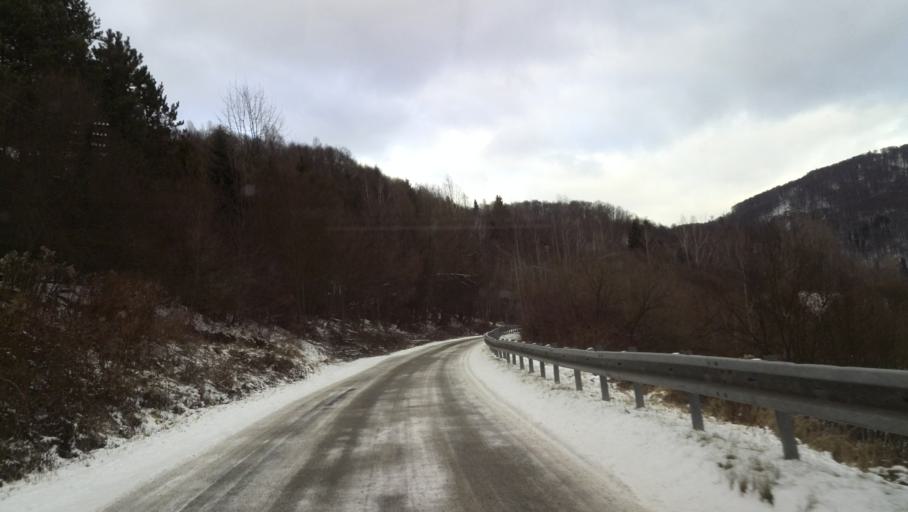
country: SK
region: Kosicky
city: Gelnica
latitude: 48.8255
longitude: 21.0656
